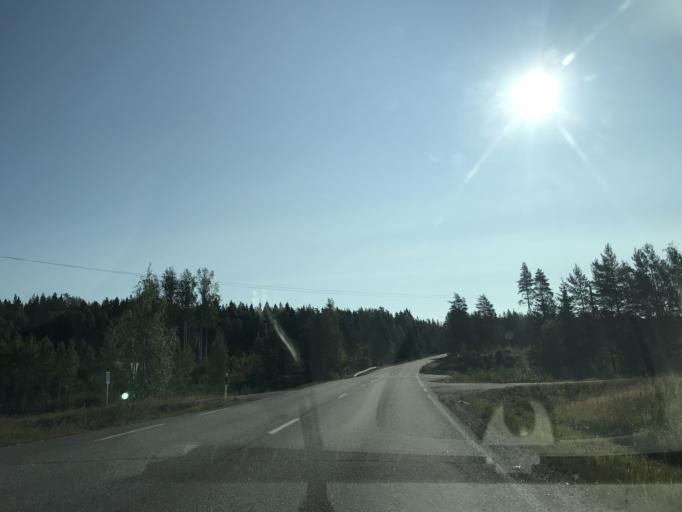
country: FI
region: Paijanne Tavastia
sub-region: Lahti
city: Orimattila
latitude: 60.7914
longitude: 25.6477
